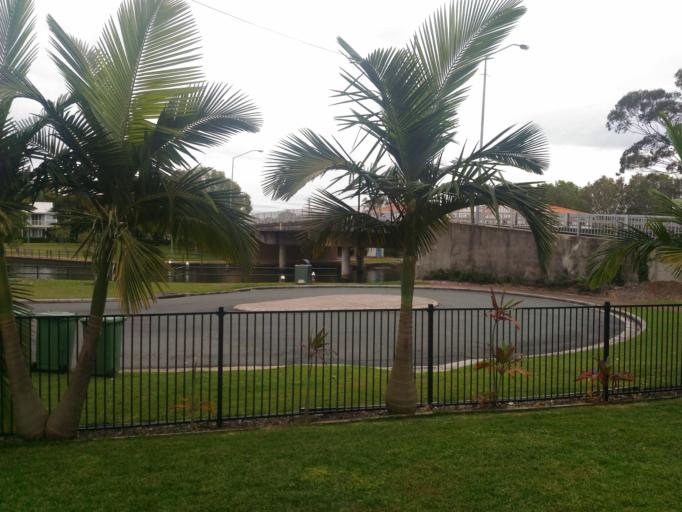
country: AU
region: Queensland
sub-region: Sunshine Coast
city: Noosaville
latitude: -26.3988
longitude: 153.0554
